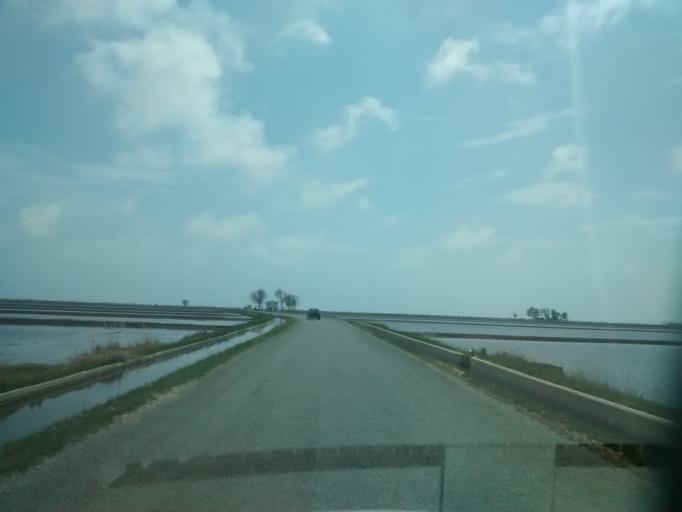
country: ES
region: Catalonia
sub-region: Provincia de Tarragona
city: Deltebre
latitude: 40.6808
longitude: 0.7966
